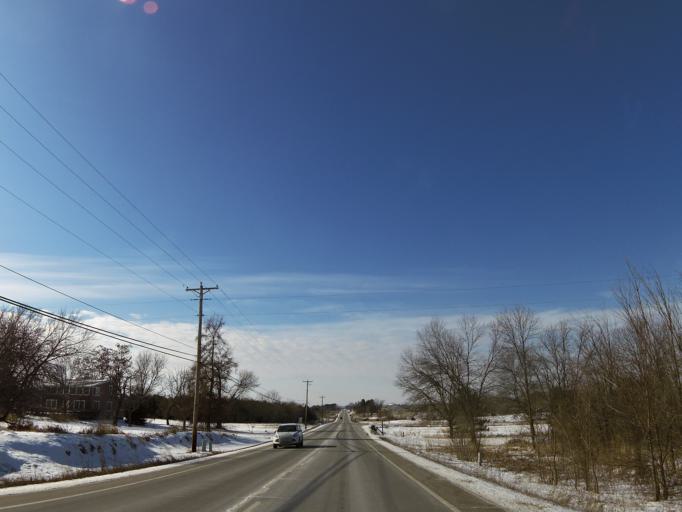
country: US
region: Wisconsin
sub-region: Saint Croix County
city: Roberts
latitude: 44.9888
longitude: -92.6477
